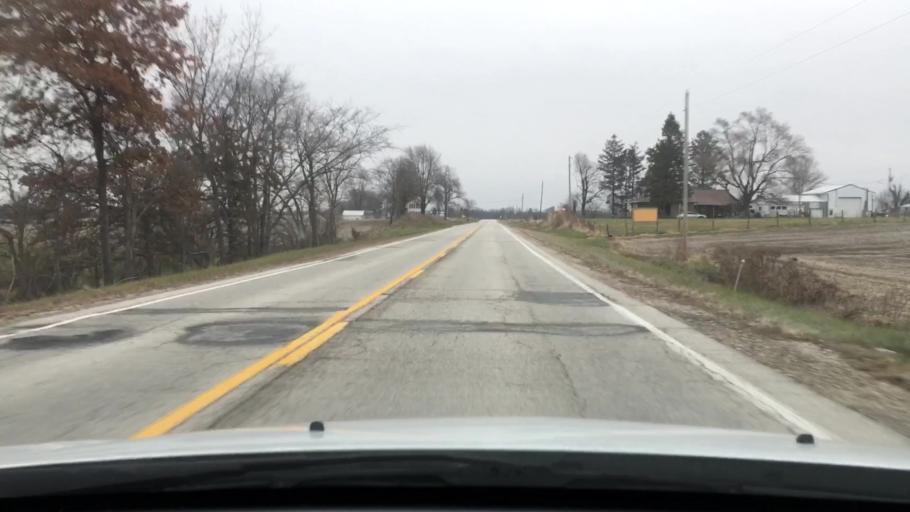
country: US
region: Illinois
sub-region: Pike County
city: Pittsfield
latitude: 39.5834
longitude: -90.9013
